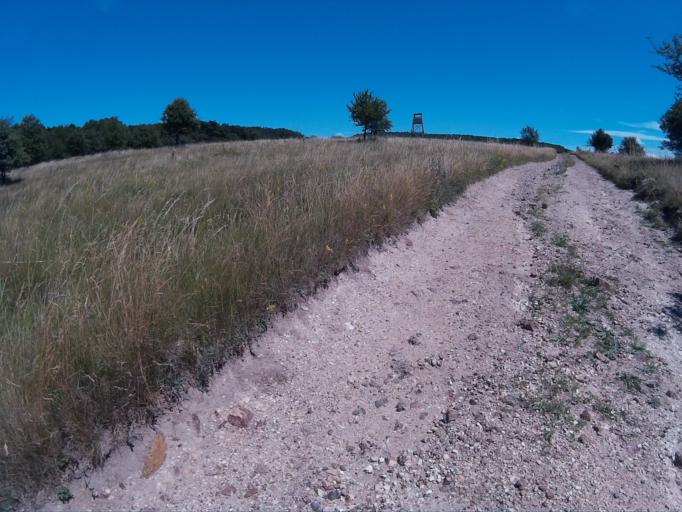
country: HU
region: Veszprem
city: Urkut
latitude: 47.1231
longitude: 17.6626
